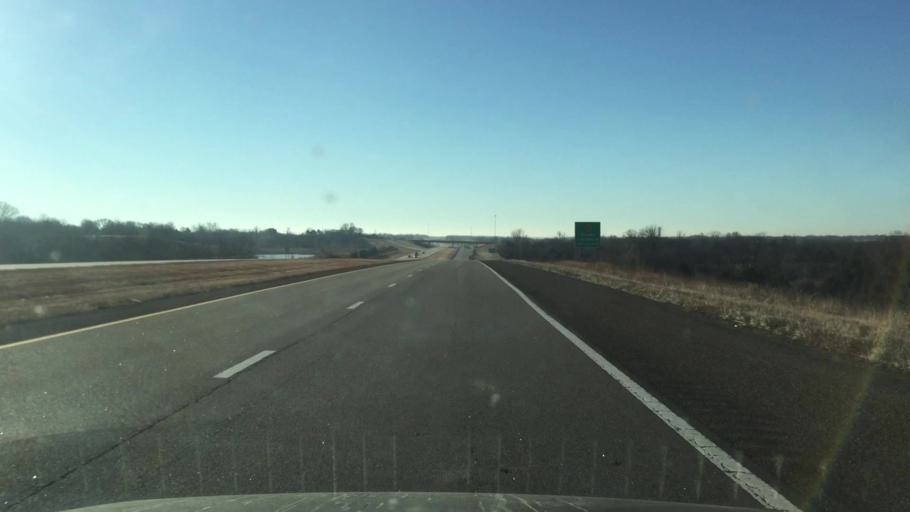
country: US
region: Kansas
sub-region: Miami County
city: Paola
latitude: 38.6311
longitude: -94.8361
